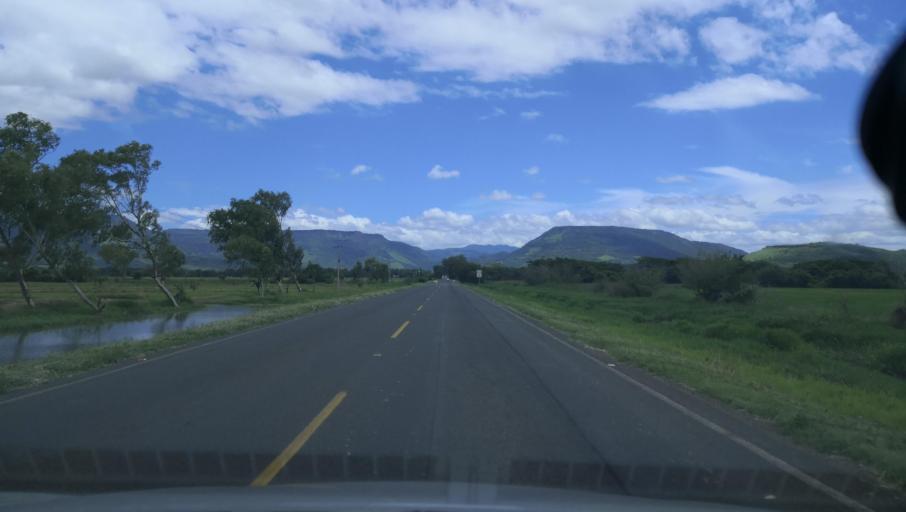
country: NI
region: Matagalpa
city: Ciudad Dario
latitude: 12.9002
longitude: -86.1626
